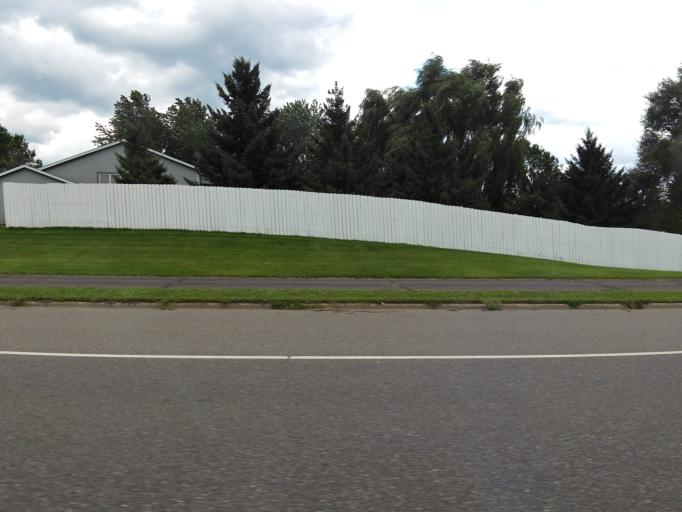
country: US
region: Minnesota
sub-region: Dakota County
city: Apple Valley
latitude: 44.7173
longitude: -93.1849
